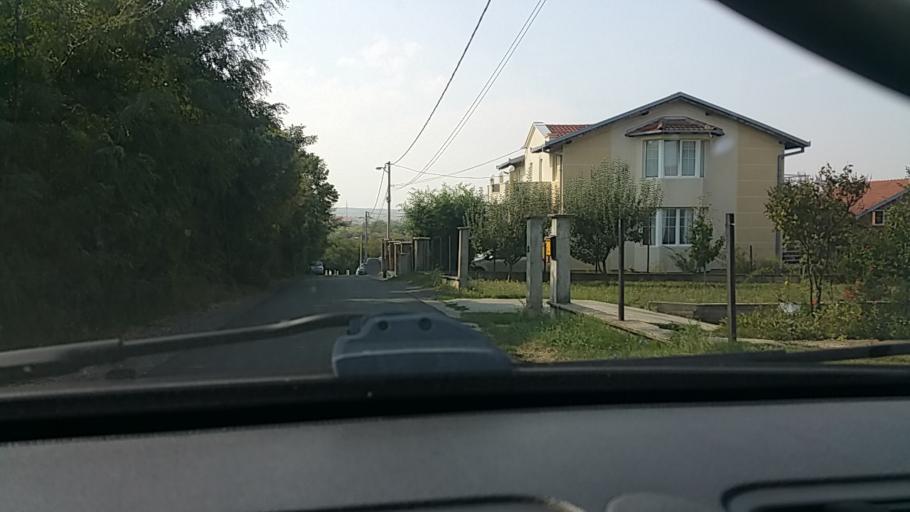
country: RS
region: Central Serbia
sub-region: Belgrade
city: Rakovica
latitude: 44.7367
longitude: 20.4578
